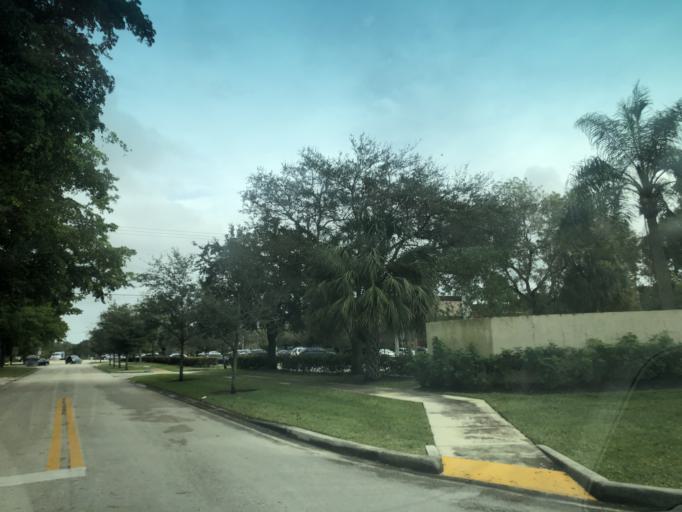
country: US
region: Florida
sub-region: Broward County
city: Coral Springs
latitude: 26.2510
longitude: -80.2549
